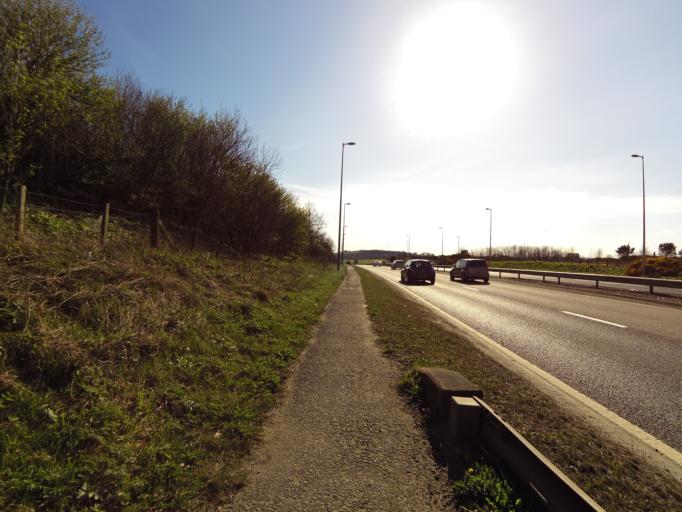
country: GB
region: Scotland
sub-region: Aberdeenshire
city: Newtonhill
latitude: 57.0307
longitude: -2.1604
